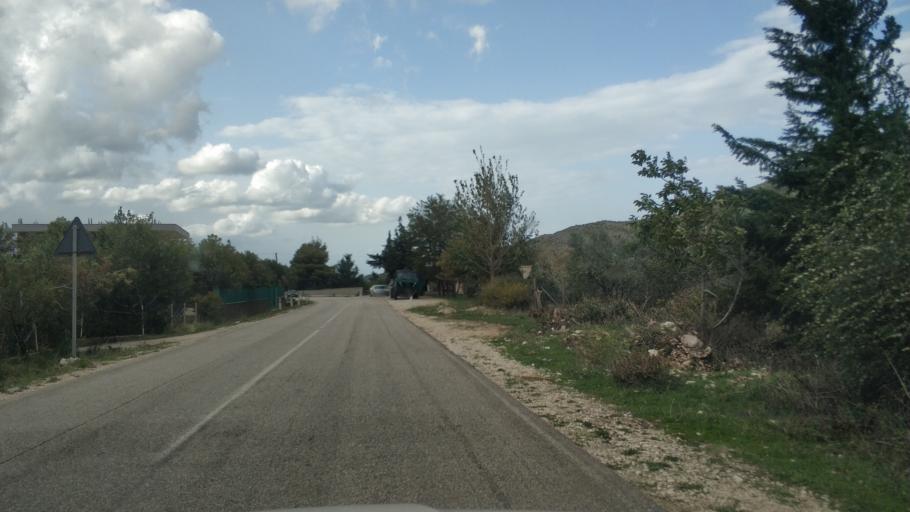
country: AL
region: Vlore
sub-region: Rrethi i Vlores
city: Orikum
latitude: 40.2714
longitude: 19.5128
